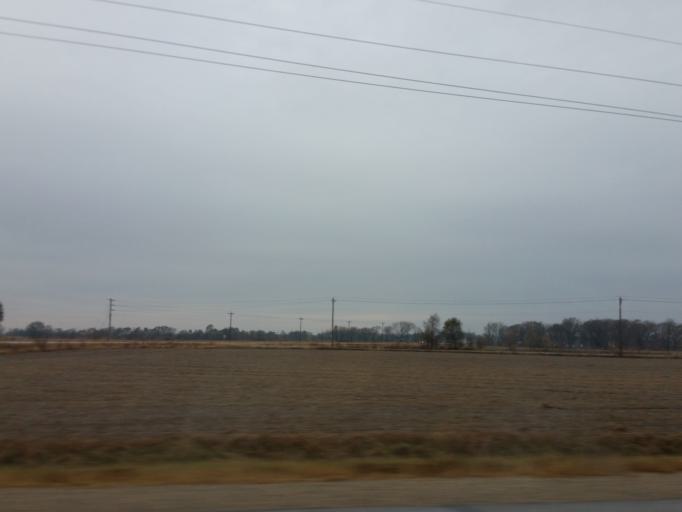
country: US
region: Iowa
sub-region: Black Hawk County
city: Elk Run Heights
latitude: 42.4001
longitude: -92.2573
